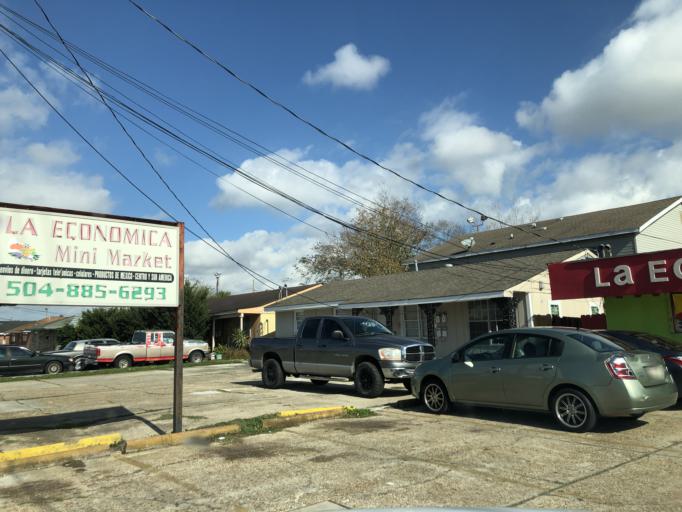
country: US
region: Louisiana
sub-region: Jefferson Parish
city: Kenner
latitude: 30.0022
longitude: -90.2196
